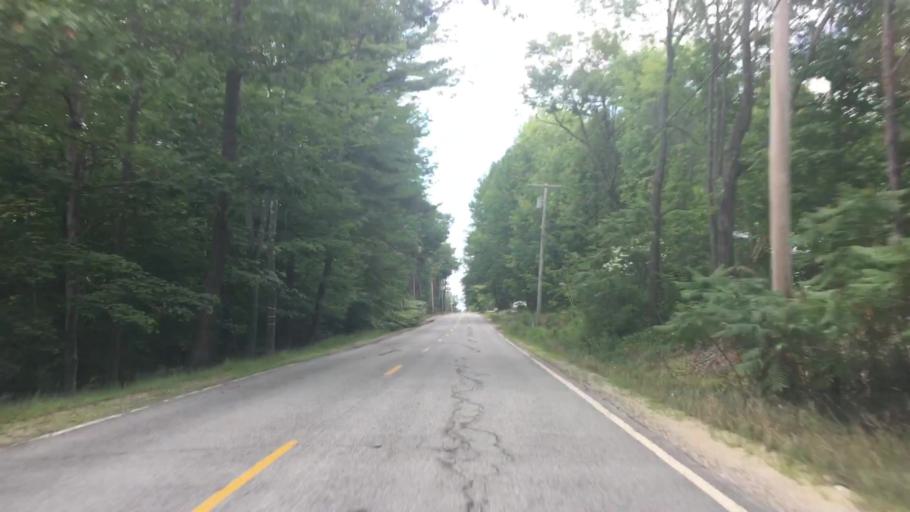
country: US
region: Maine
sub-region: Oxford County
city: Oxford
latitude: 44.0432
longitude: -70.5428
